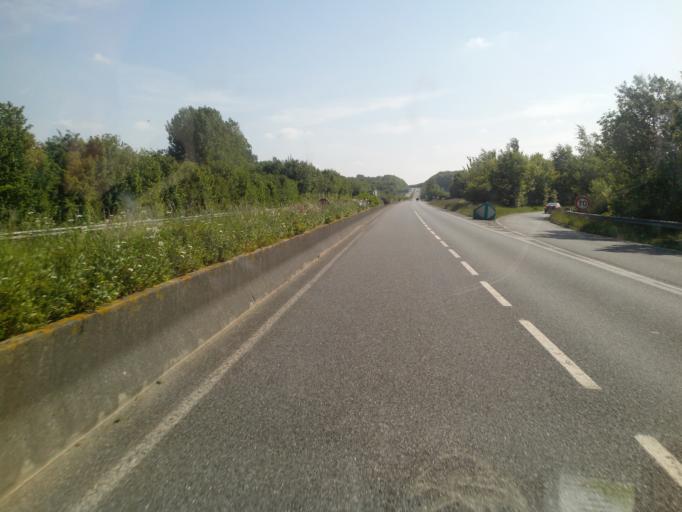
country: FR
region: Picardie
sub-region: Departement de la Somme
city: Abbeville
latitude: 50.1101
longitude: 1.7898
